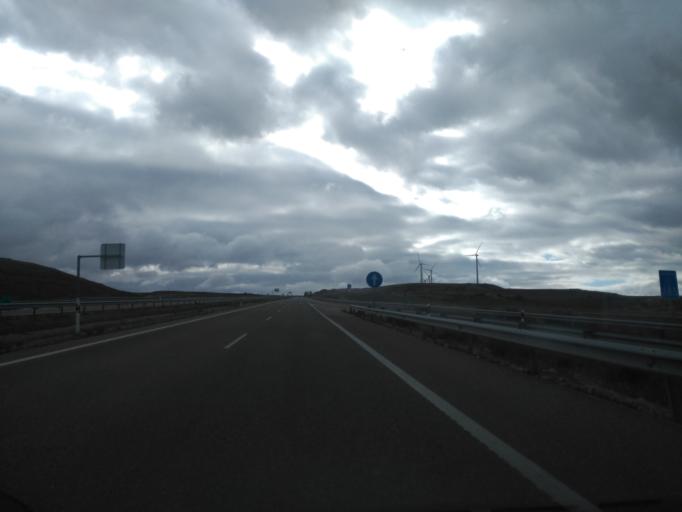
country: ES
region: Castille and Leon
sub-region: Provincia de Palencia
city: Monzon de Campos
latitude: 42.1143
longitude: -4.4810
